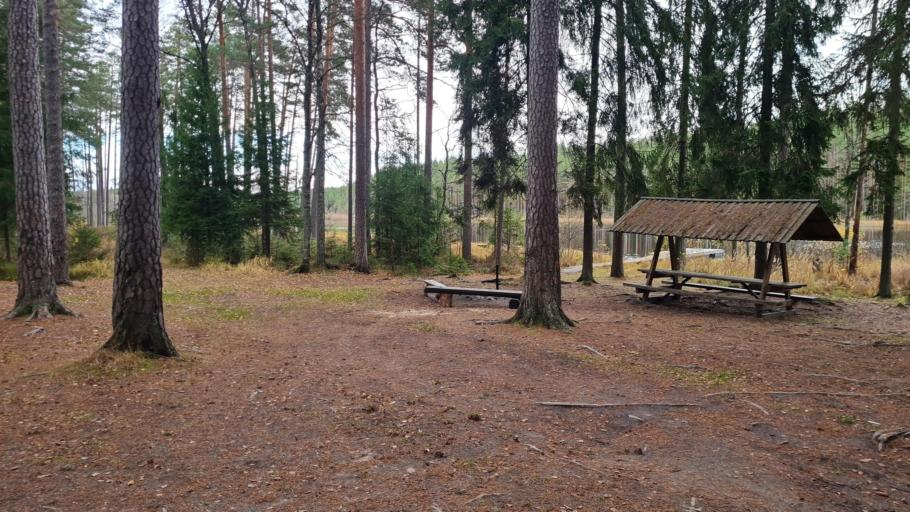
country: EE
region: Polvamaa
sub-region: Polva linn
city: Polva
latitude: 58.1482
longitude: 27.1376
